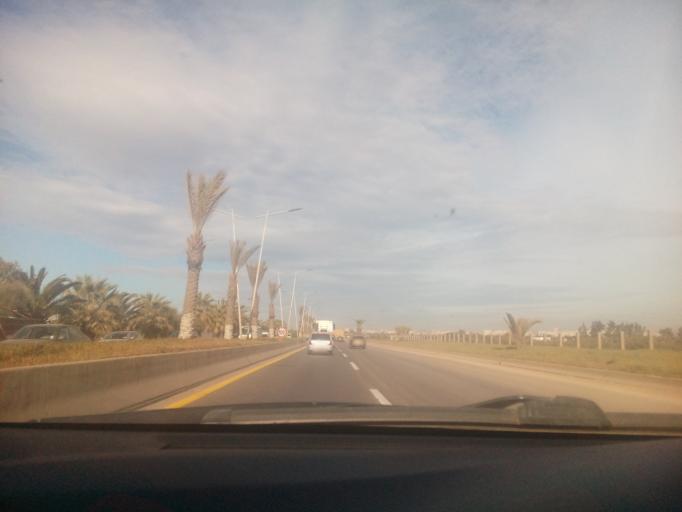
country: DZ
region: Oran
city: Es Senia
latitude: 35.6543
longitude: -0.5919
